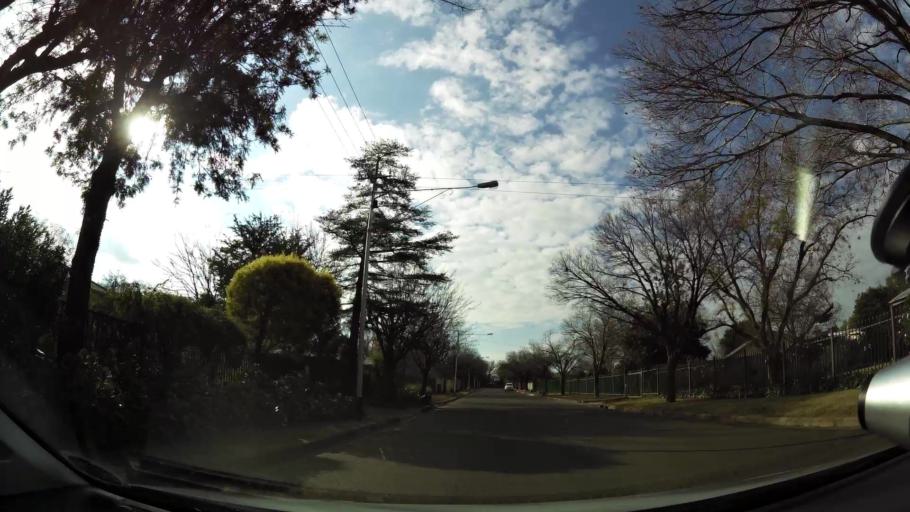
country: ZA
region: Orange Free State
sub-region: Mangaung Metropolitan Municipality
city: Bloemfontein
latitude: -29.0801
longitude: 26.2139
